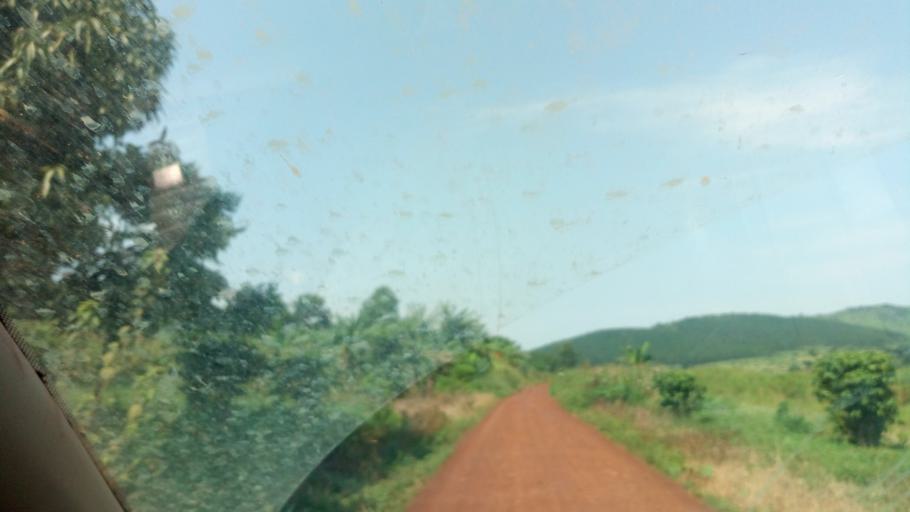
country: UG
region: Western Region
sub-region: Masindi District
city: Masindi
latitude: 1.6548
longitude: 31.8087
